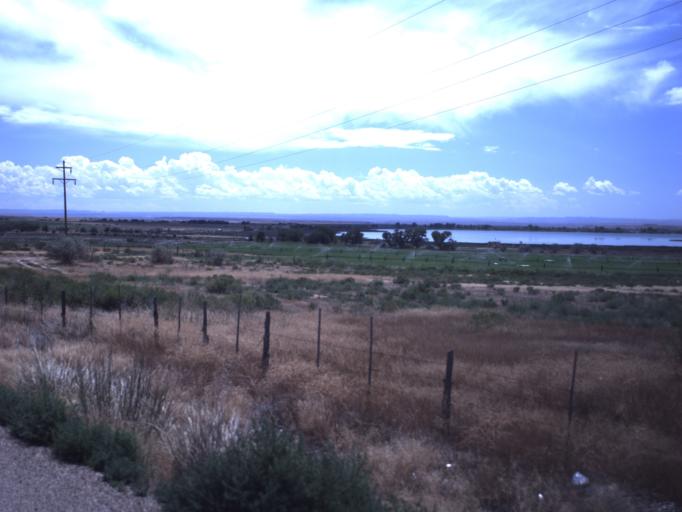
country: US
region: Utah
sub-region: Uintah County
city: Naples
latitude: 40.2136
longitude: -109.6730
